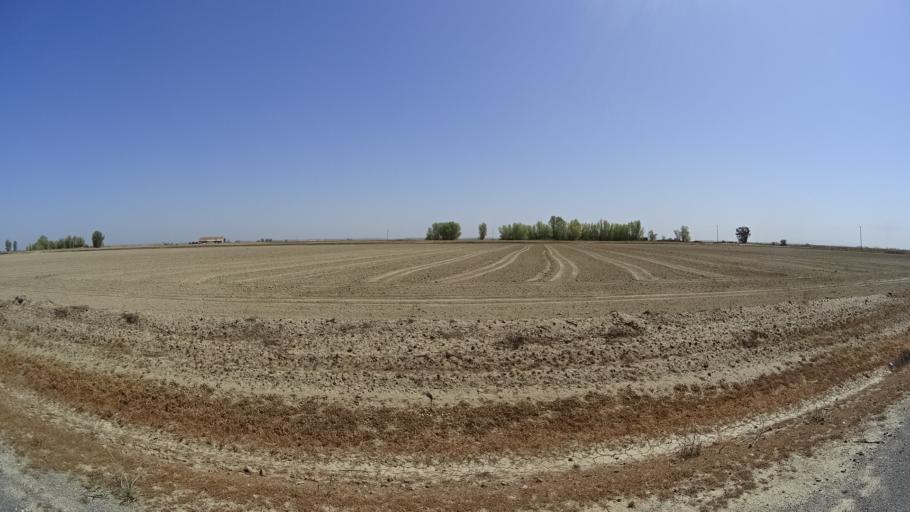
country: US
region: California
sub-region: Glenn County
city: Willows
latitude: 39.5014
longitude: -122.1030
